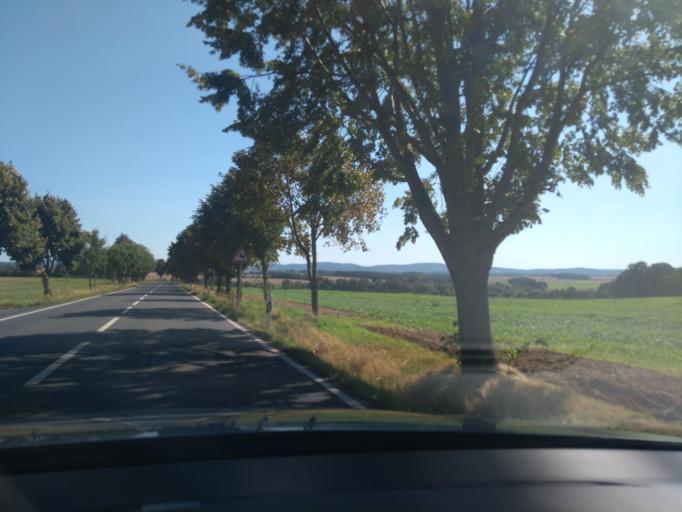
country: DE
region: Saxony
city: Goda
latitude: 51.2091
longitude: 14.2908
